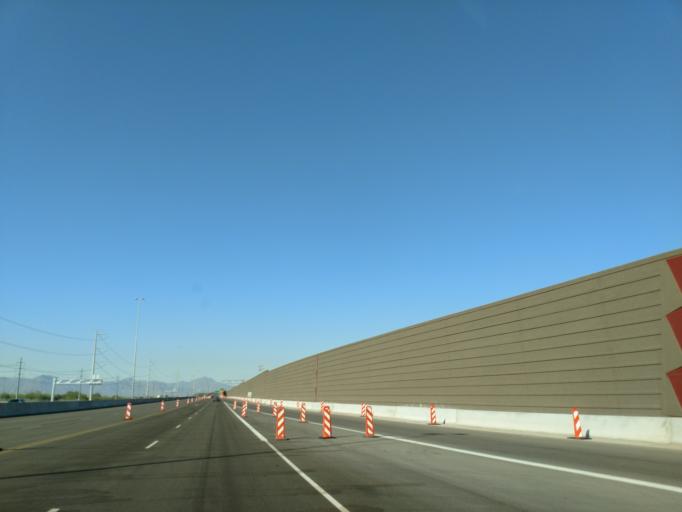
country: US
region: Arizona
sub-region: Maricopa County
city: Guadalupe
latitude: 33.2919
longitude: -112.0015
